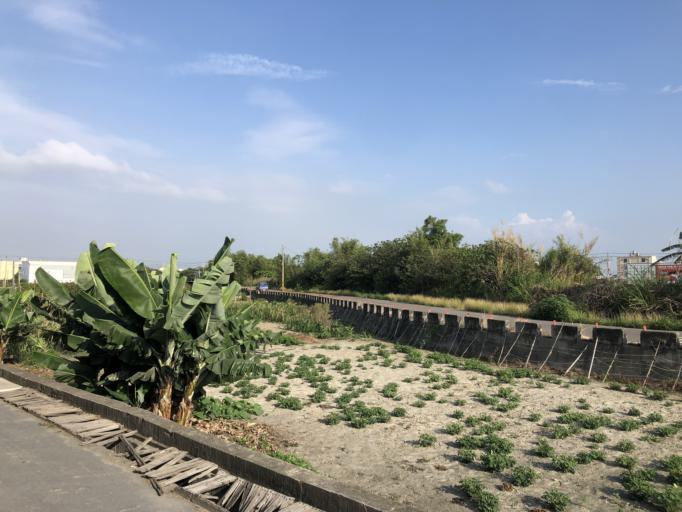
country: TW
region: Taiwan
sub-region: Changhua
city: Chang-hua
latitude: 24.0498
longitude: 120.4694
